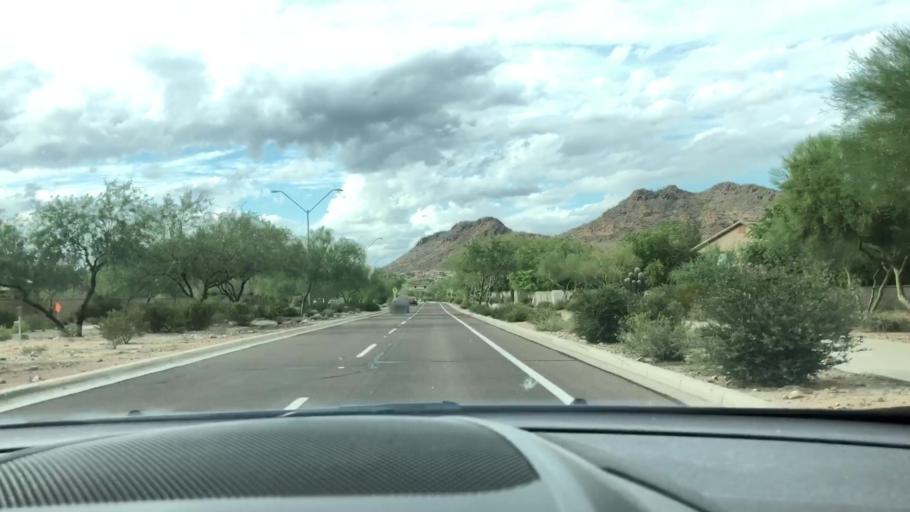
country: US
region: Arizona
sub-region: Maricopa County
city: Sun City West
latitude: 33.7254
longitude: -112.2412
